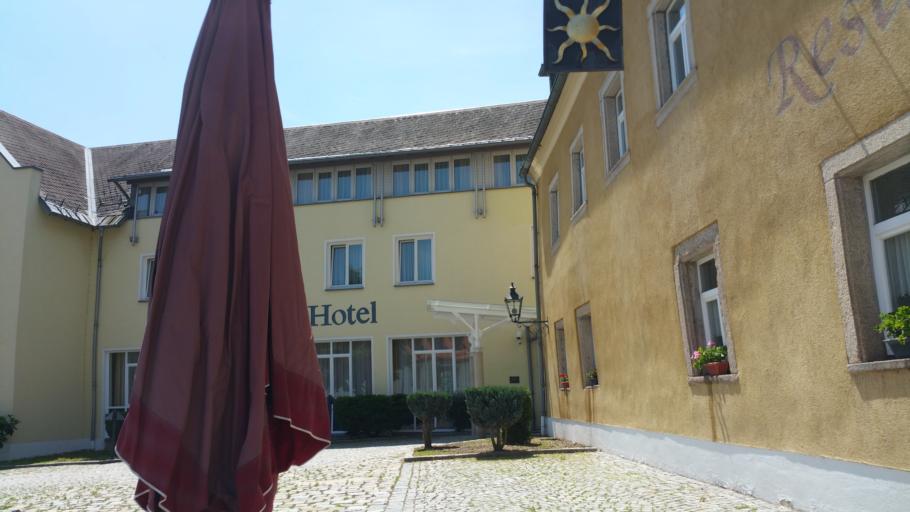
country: DE
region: Bavaria
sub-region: Upper Franconia
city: Schwarzenbach an der Saale
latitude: 50.2227
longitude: 11.9318
